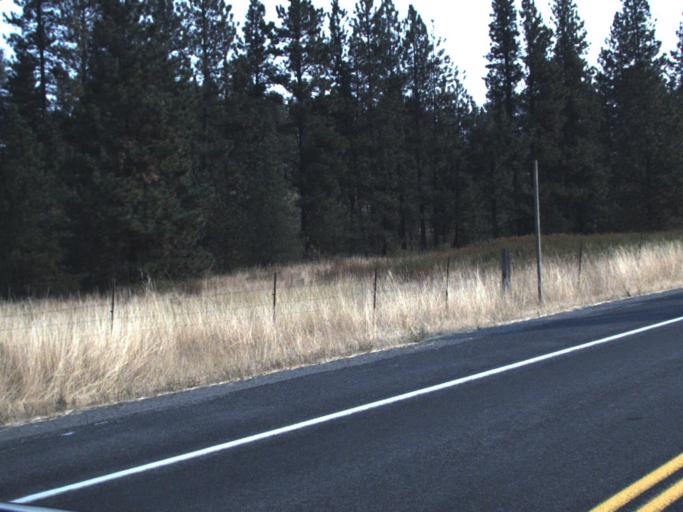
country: US
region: Washington
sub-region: Spokane County
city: Veradale
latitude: 47.4445
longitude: -117.1206
